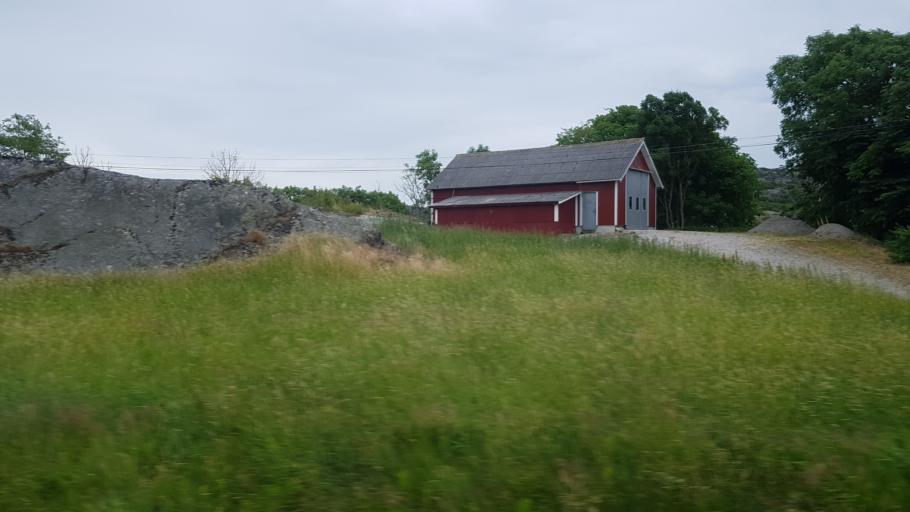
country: SE
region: Vaestra Goetaland
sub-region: Tjorns Kommun
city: Skaerhamn
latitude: 57.9780
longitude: 11.5636
